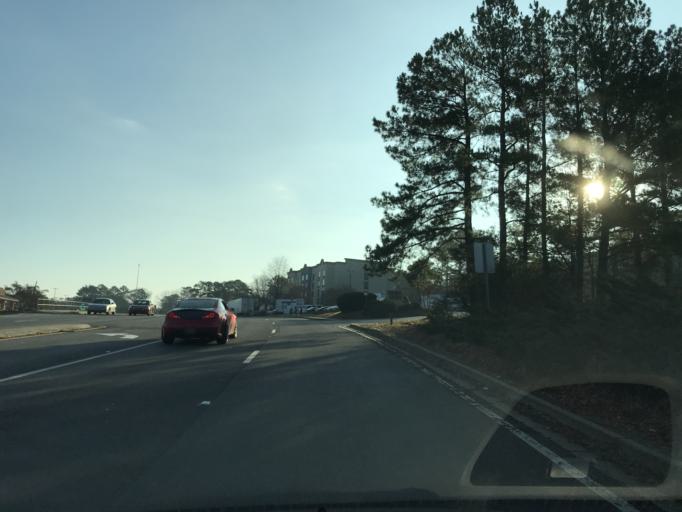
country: US
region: Georgia
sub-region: Fulton County
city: College Park
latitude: 33.6145
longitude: -84.4420
